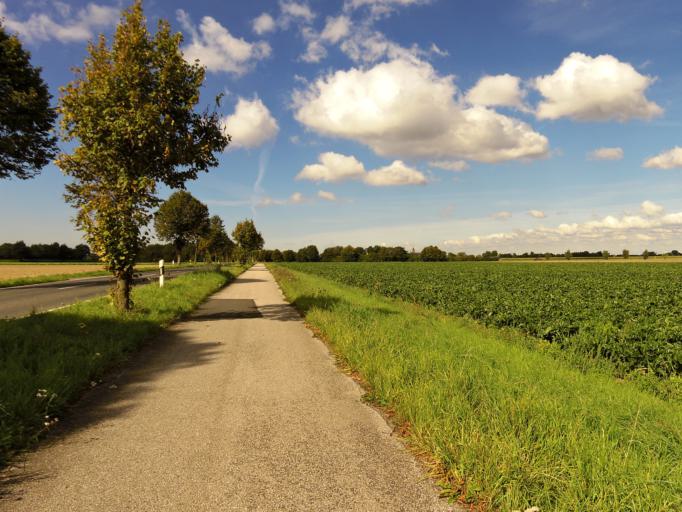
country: DE
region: North Rhine-Westphalia
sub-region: Regierungsbezirk Koln
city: Euskirchen
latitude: 50.6406
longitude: 6.8469
